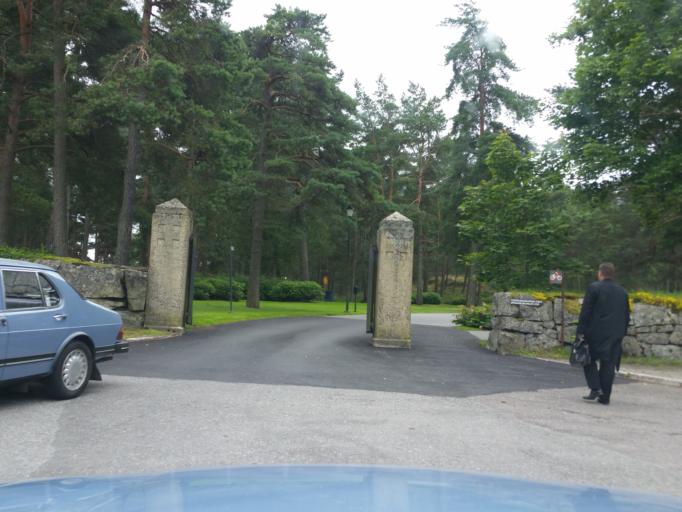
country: FI
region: Varsinais-Suomi
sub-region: Turku
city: Turku
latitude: 60.4354
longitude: 22.3120
